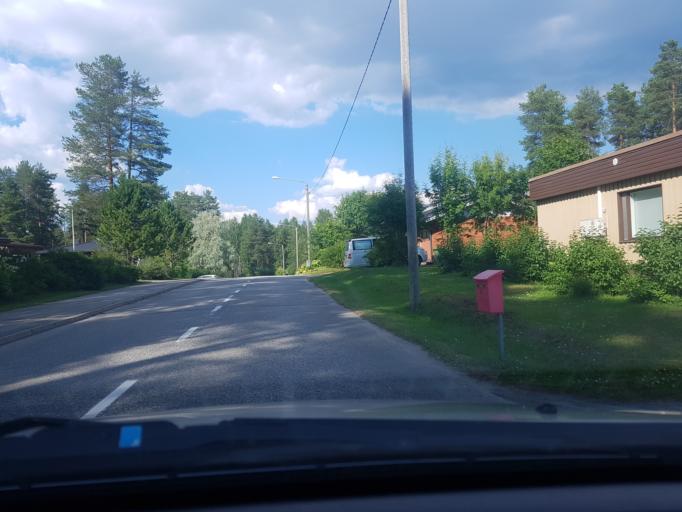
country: FI
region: Kainuu
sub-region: Kehys-Kainuu
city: Kuhmo
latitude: 64.1292
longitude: 29.5433
